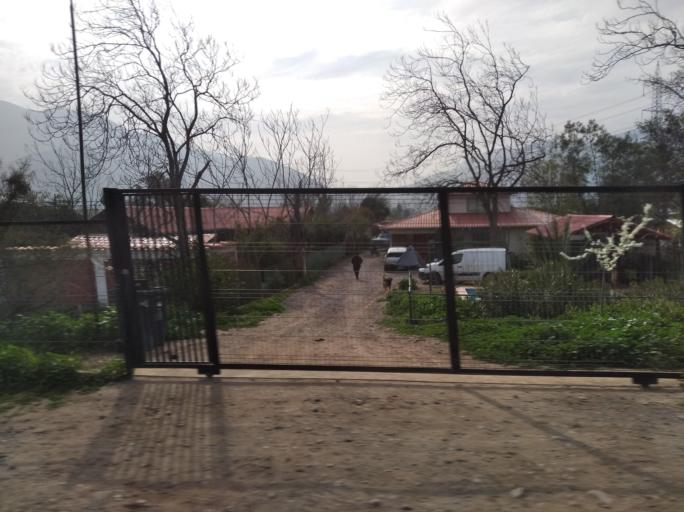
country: CL
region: Santiago Metropolitan
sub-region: Provincia de Chacabuco
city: Lampa
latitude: -33.2631
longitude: -70.8976
